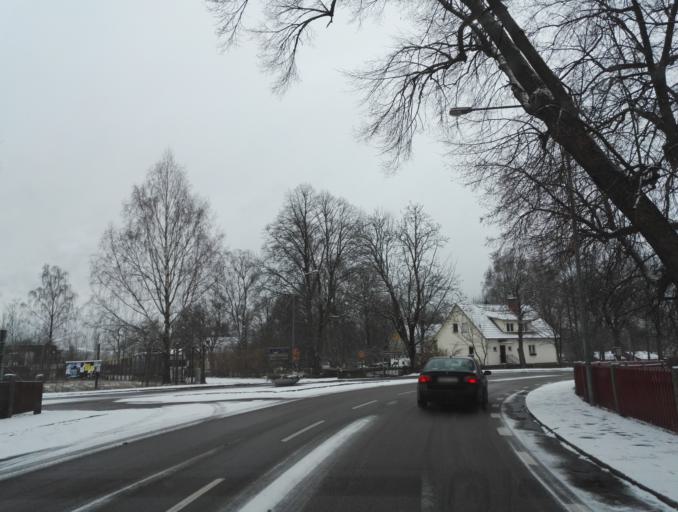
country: SE
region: Kronoberg
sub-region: Lessebo Kommun
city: Lessebo
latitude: 56.7502
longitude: 15.2736
